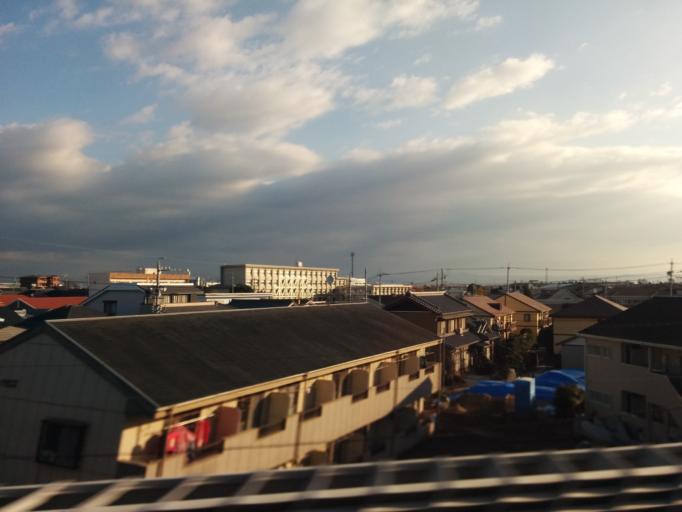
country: JP
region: Aichi
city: Chiryu
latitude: 34.9848
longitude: 137.0452
